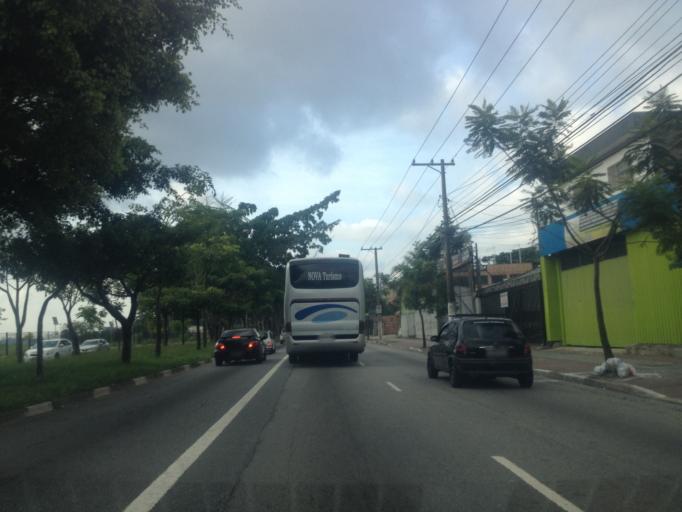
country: BR
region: Sao Paulo
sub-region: Diadema
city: Diadema
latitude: -23.6919
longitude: -46.7146
